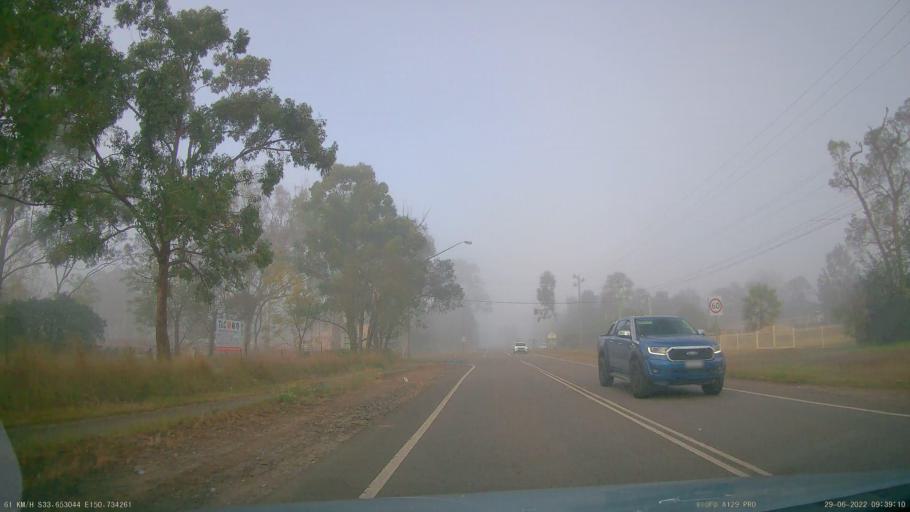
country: AU
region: New South Wales
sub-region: Hawkesbury
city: Richmond
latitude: -33.6534
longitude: 150.7342
